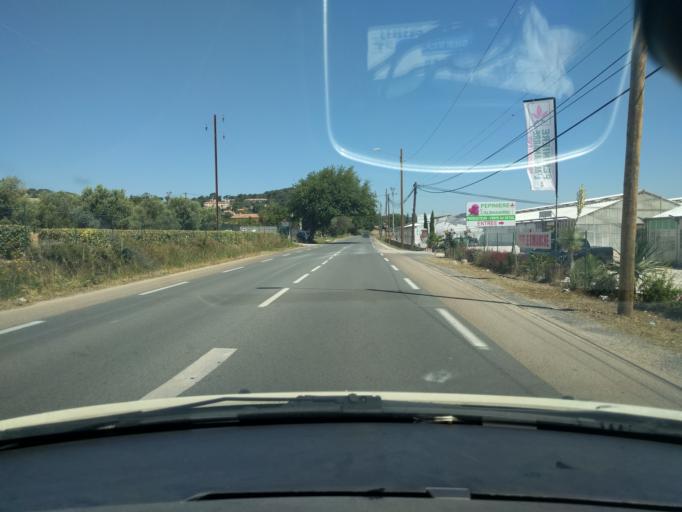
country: FR
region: Provence-Alpes-Cote d'Azur
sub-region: Departement du Var
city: Hyeres
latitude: 43.0874
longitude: 6.1286
